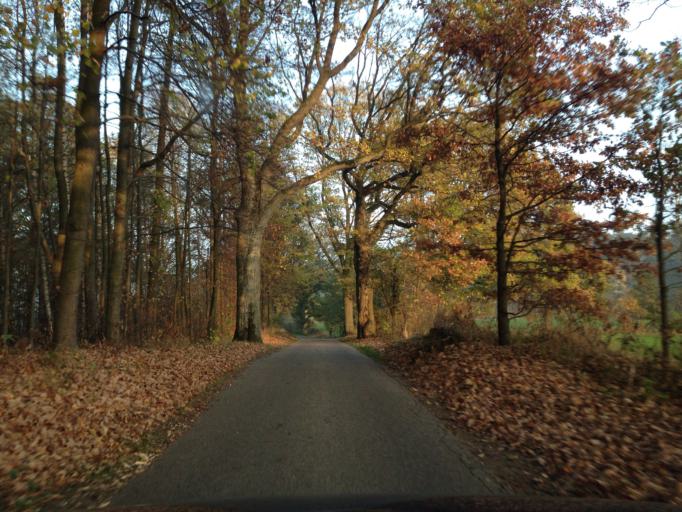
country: PL
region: Warmian-Masurian Voivodeship
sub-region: Powiat dzialdowski
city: Lidzbark
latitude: 53.2476
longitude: 19.7621
